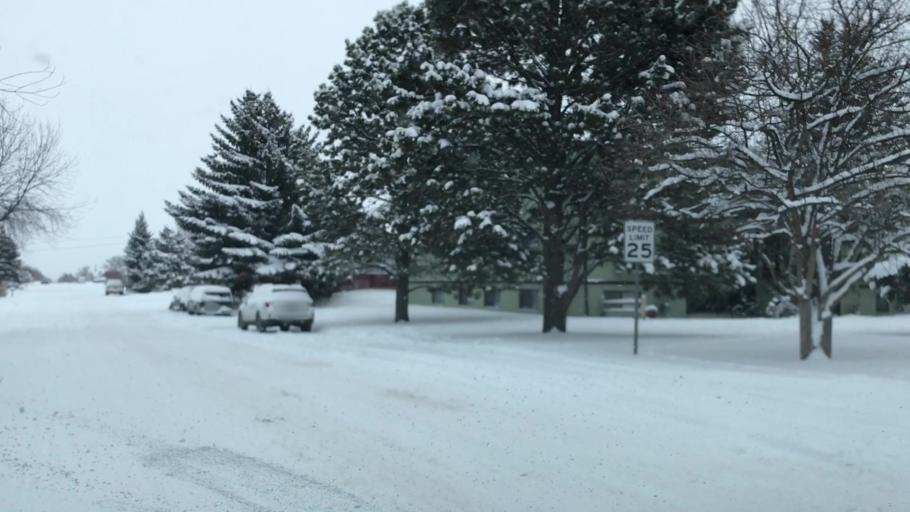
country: US
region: Montana
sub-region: Lewis and Clark County
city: Helena
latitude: 46.5932
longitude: -112.0160
